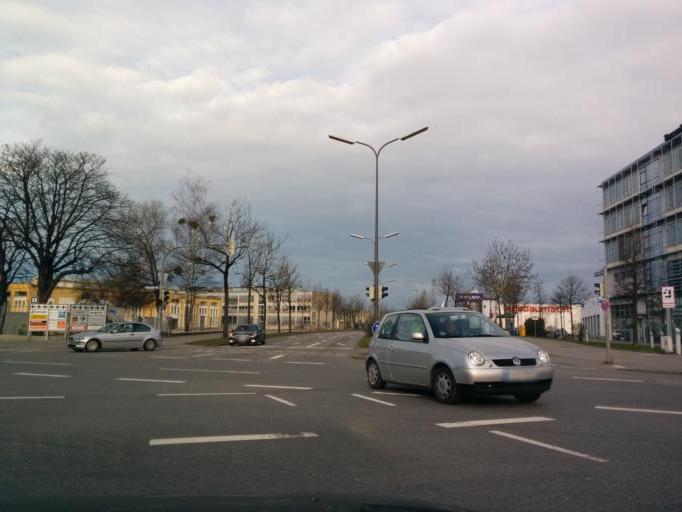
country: DE
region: Bavaria
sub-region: Upper Bavaria
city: Munich
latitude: 48.1860
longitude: 11.5517
